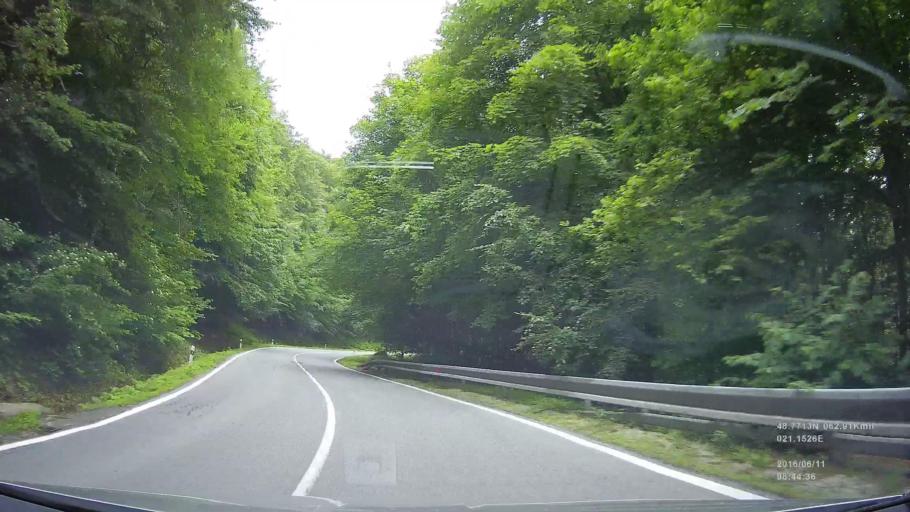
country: SK
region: Kosicky
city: Kosice
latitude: 48.7528
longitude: 21.1994
